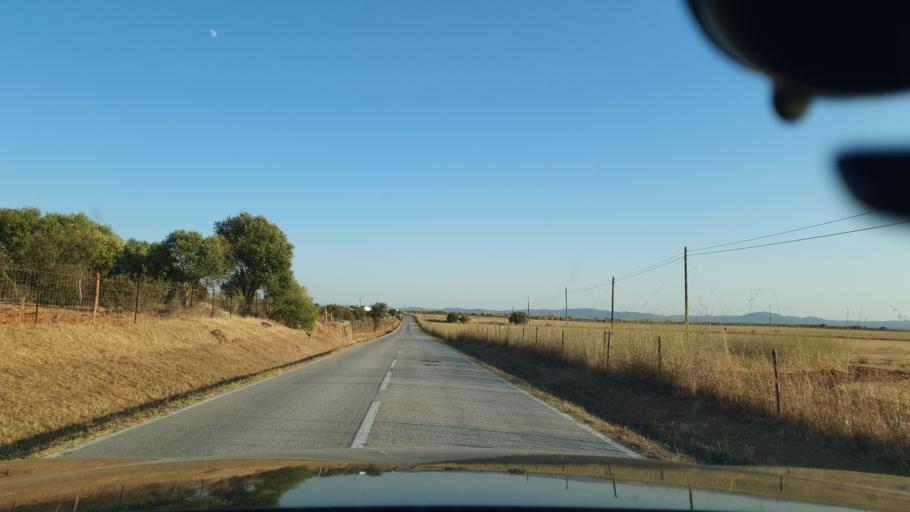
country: PT
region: Evora
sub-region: Estremoz
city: Estremoz
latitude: 38.9016
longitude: -7.6677
